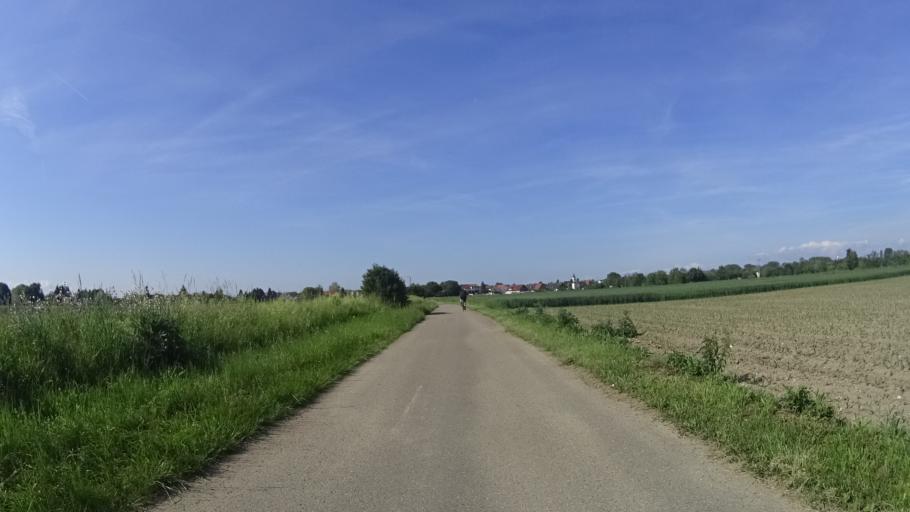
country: DE
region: Baden-Wuerttemberg
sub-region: Freiburg Region
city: Kehl
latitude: 48.5279
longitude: 7.8271
